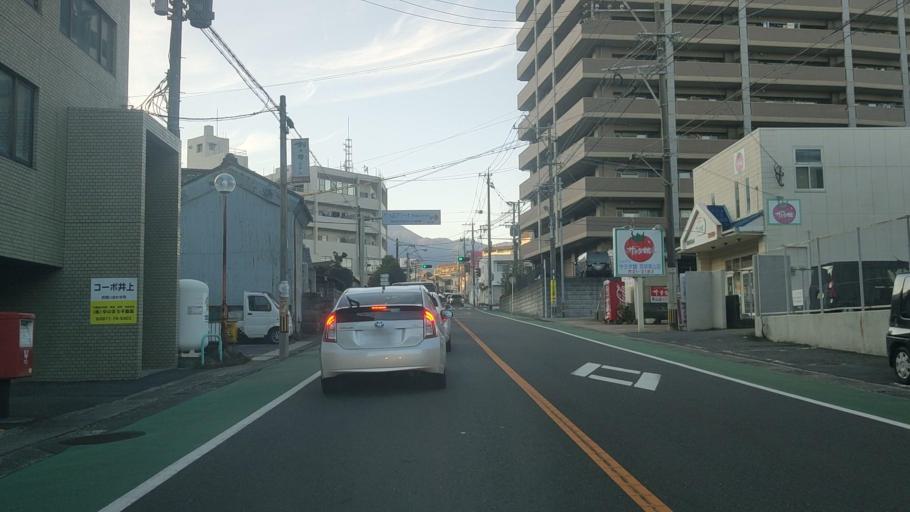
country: JP
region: Oita
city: Beppu
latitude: 33.2764
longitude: 131.4916
